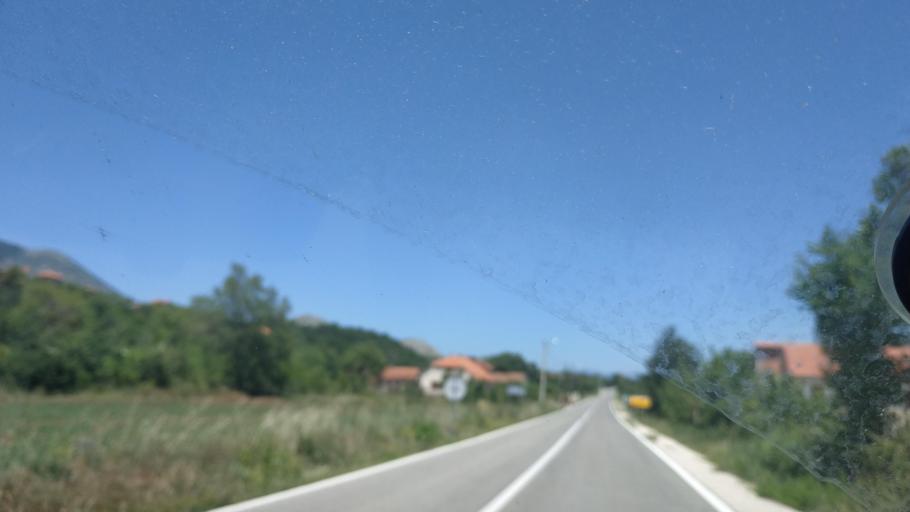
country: HR
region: Sibensko-Kniniska
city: Drnis
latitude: 43.8813
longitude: 16.2042
